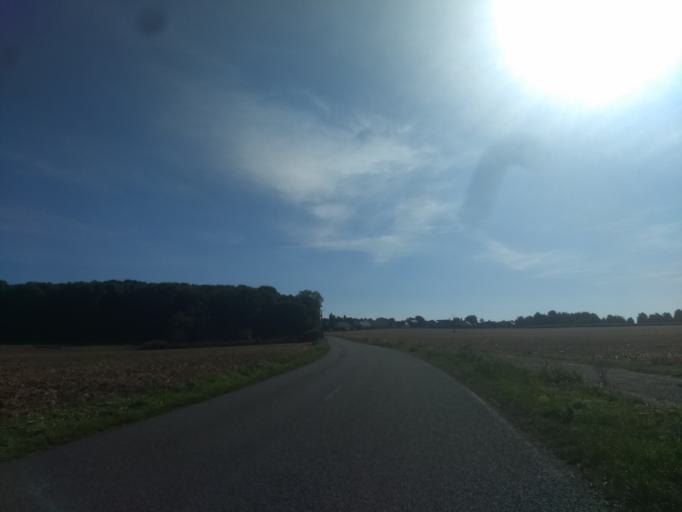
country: FR
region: Nord-Pas-de-Calais
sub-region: Departement du Pas-de-Calais
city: Roeux
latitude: 50.2775
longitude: 2.8940
